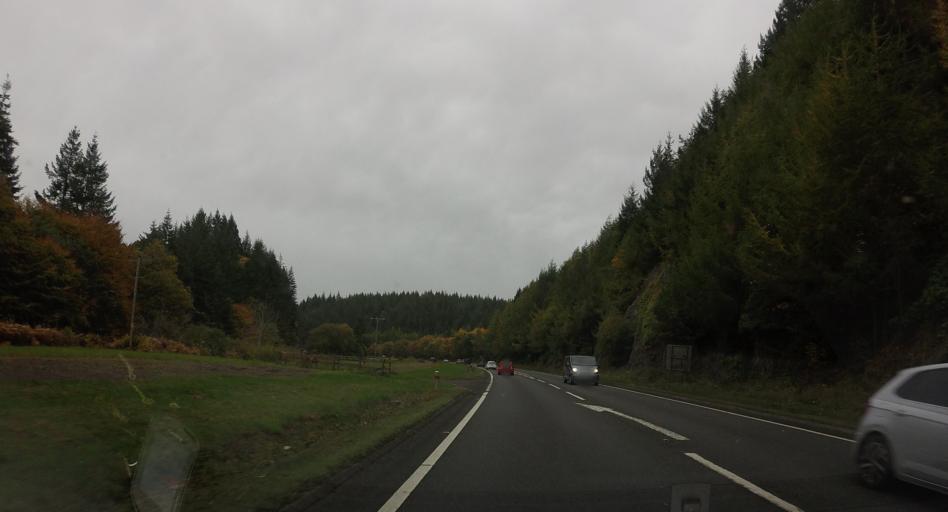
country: GB
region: Scotland
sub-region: Perth and Kinross
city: Bankfoot
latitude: 56.5651
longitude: -3.6217
